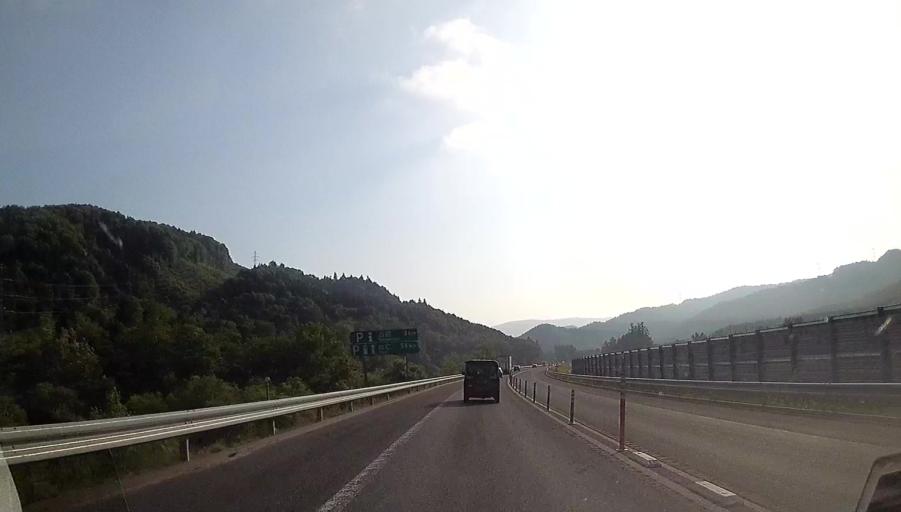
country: JP
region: Hokkaido
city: Shimo-furano
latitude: 43.0226
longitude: 142.4470
